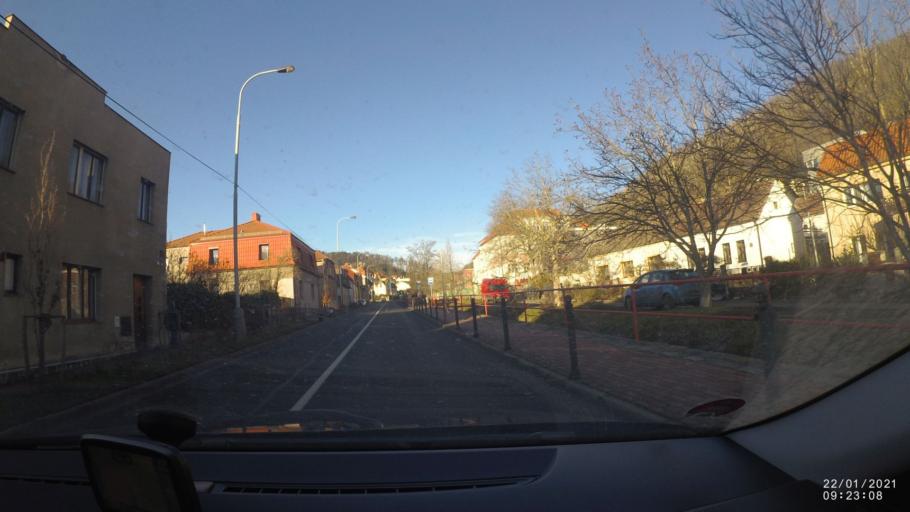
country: CZ
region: Praha
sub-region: Praha 12
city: Modrany
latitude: 50.0119
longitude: 14.3830
